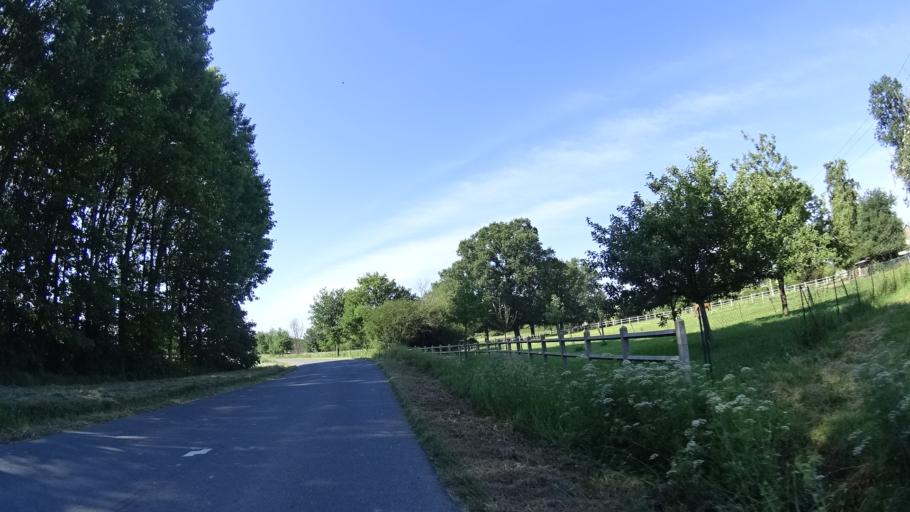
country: FR
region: Brittany
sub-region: Departement d'Ille-et-Vilaine
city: Guipry
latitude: 47.8013
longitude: -1.8487
